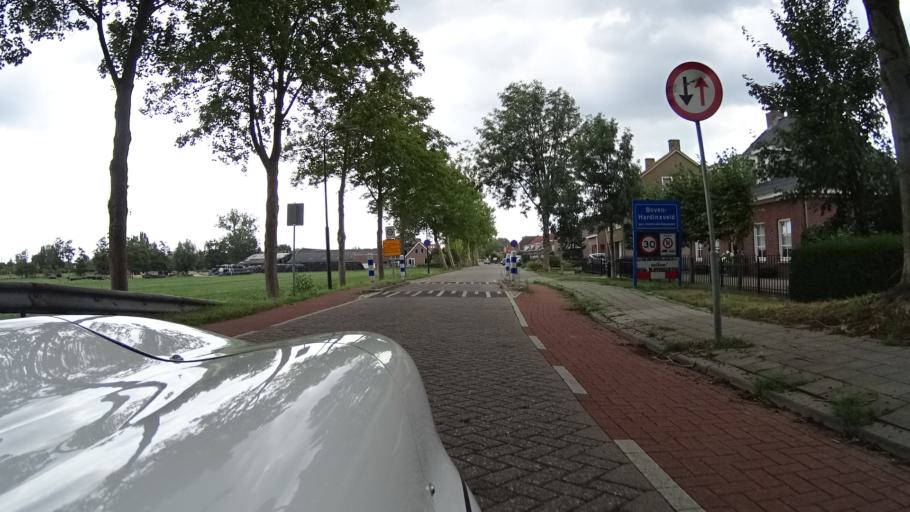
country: NL
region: South Holland
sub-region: Gemeente Hardinxveld-Giessendam
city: Boven-Hardinxveld
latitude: 51.8297
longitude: 4.8827
